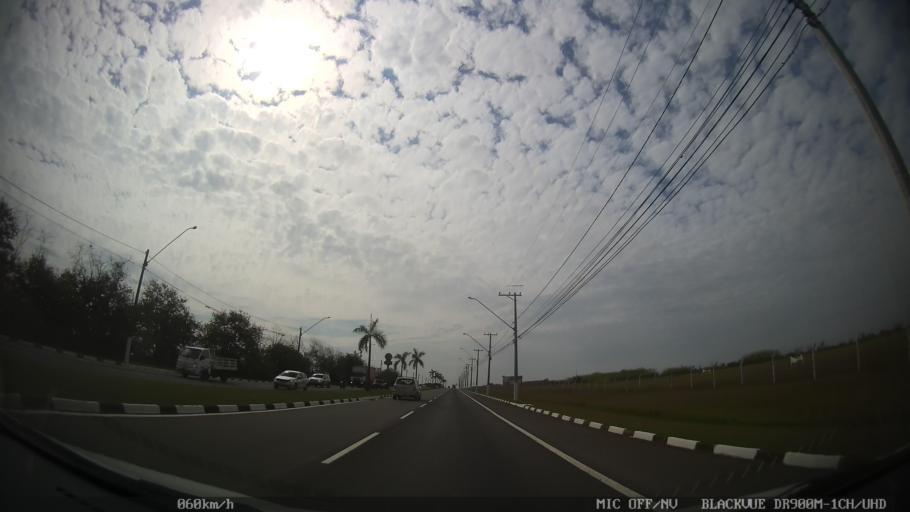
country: BR
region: Sao Paulo
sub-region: Paulinia
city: Paulinia
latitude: -22.7933
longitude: -47.1716
